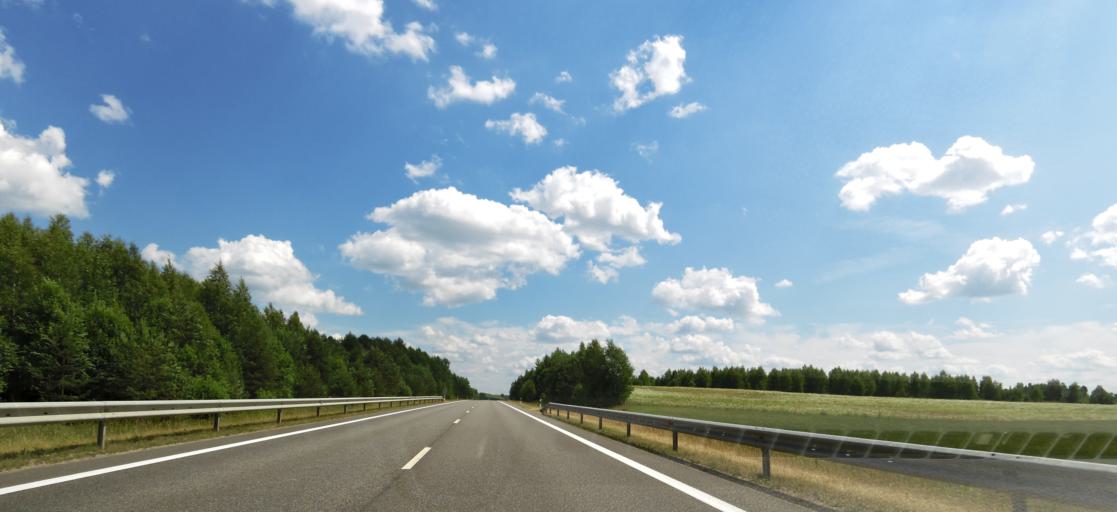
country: LT
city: Skaidiskes
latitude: 54.5859
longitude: 25.5768
